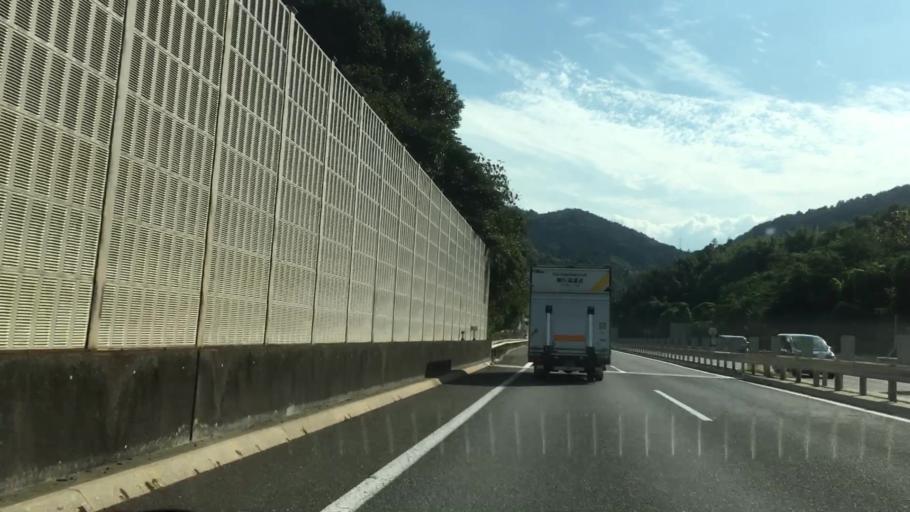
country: JP
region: Yamaguchi
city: Otake
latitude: 34.2393
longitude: 132.2147
